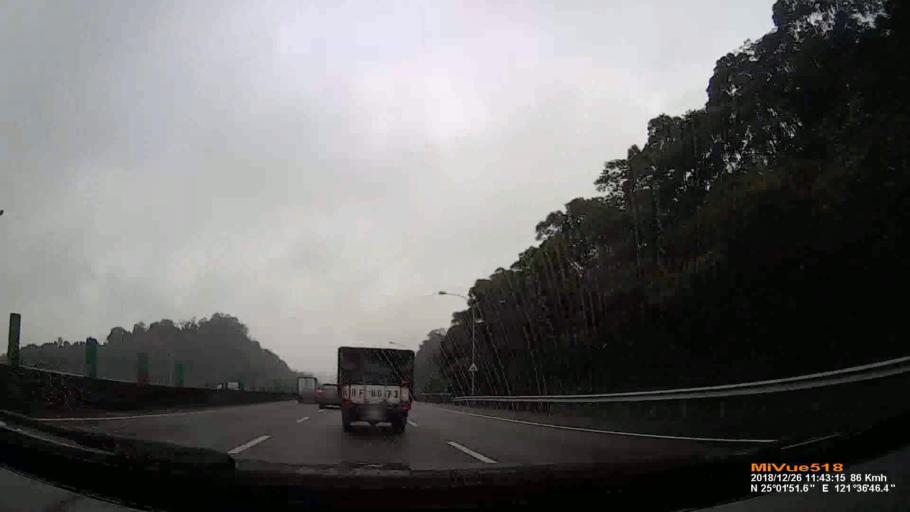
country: TW
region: Taipei
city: Taipei
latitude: 25.0350
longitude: 121.6236
